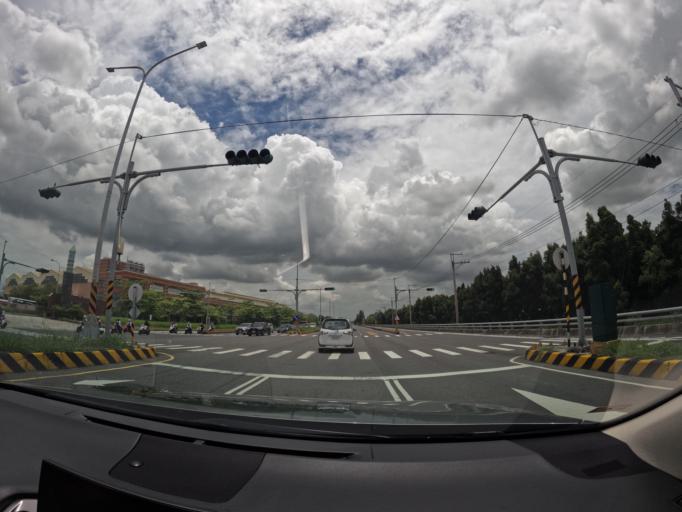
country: TW
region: Kaohsiung
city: Kaohsiung
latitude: 22.7762
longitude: 120.3006
